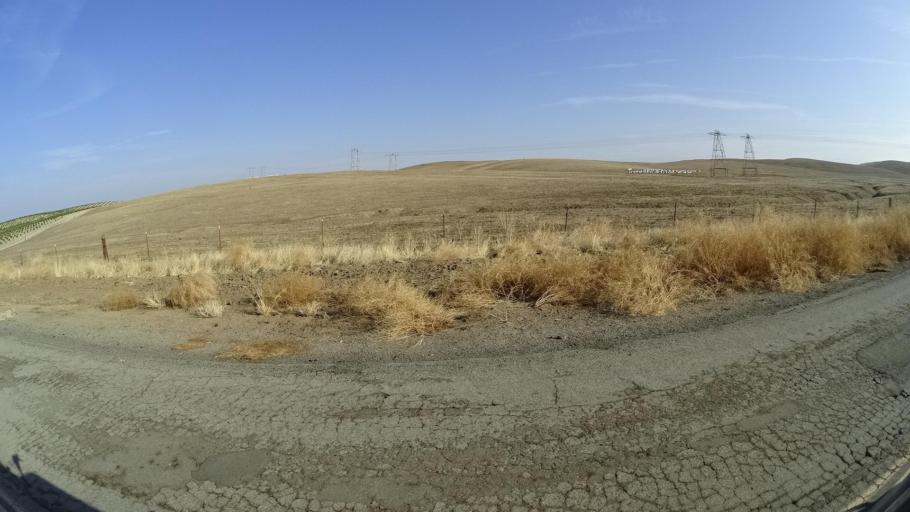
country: US
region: California
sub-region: Tulare County
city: Richgrove
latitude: 35.6410
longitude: -119.0448
